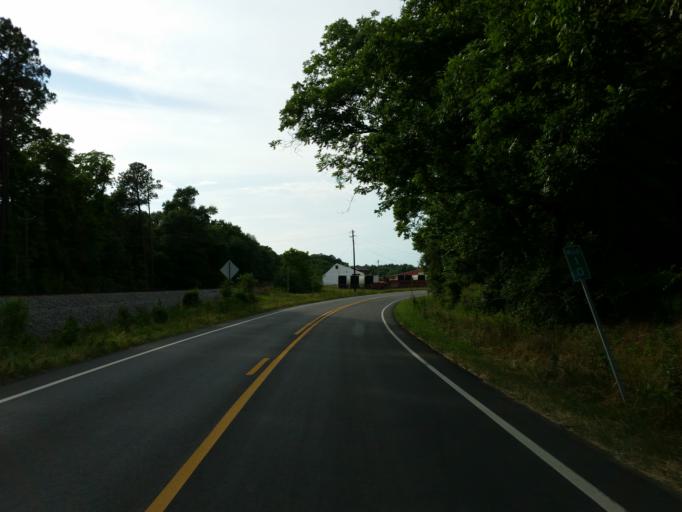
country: US
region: Georgia
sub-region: Turner County
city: Ashburn
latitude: 31.7204
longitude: -83.6632
